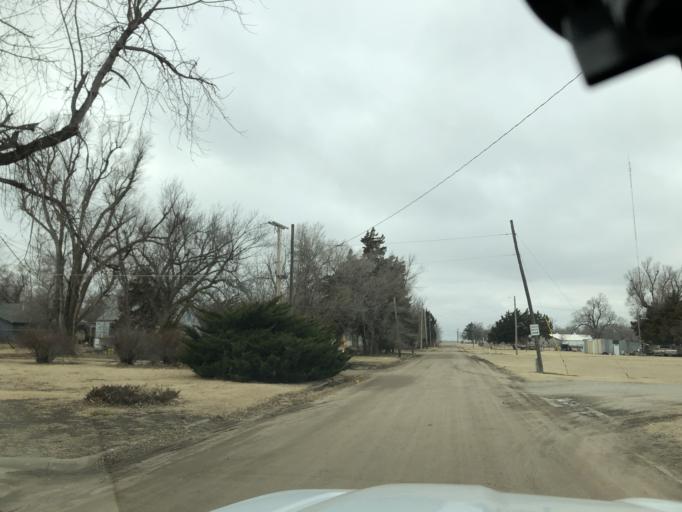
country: US
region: Kansas
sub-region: Stafford County
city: Stafford
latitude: 37.9677
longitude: -98.6021
